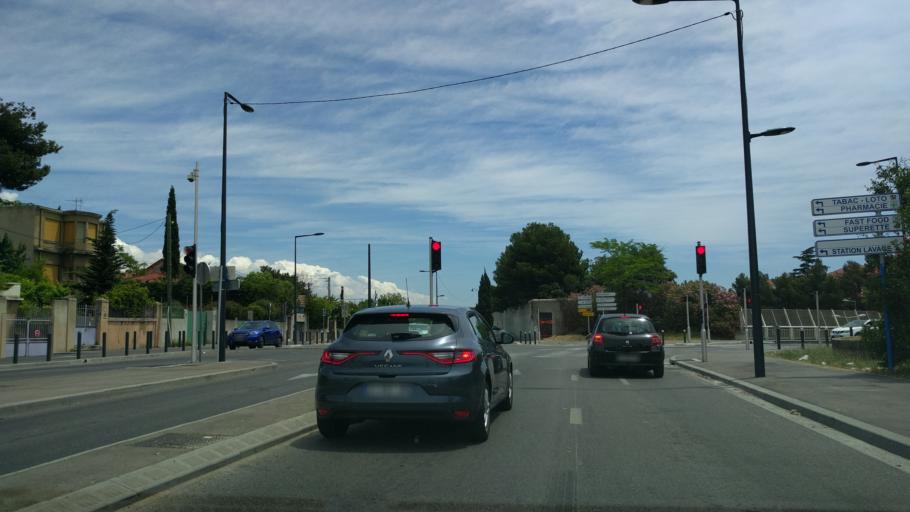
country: FR
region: Provence-Alpes-Cote d'Azur
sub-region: Departement des Bouches-du-Rhone
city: Marseille 13
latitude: 43.3299
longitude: 5.4134
